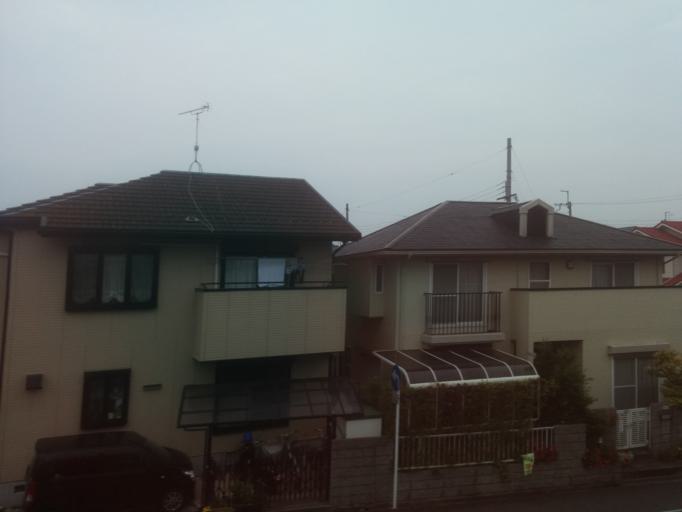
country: JP
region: Shiga Prefecture
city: Kusatsu
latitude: 35.0360
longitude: 135.9782
